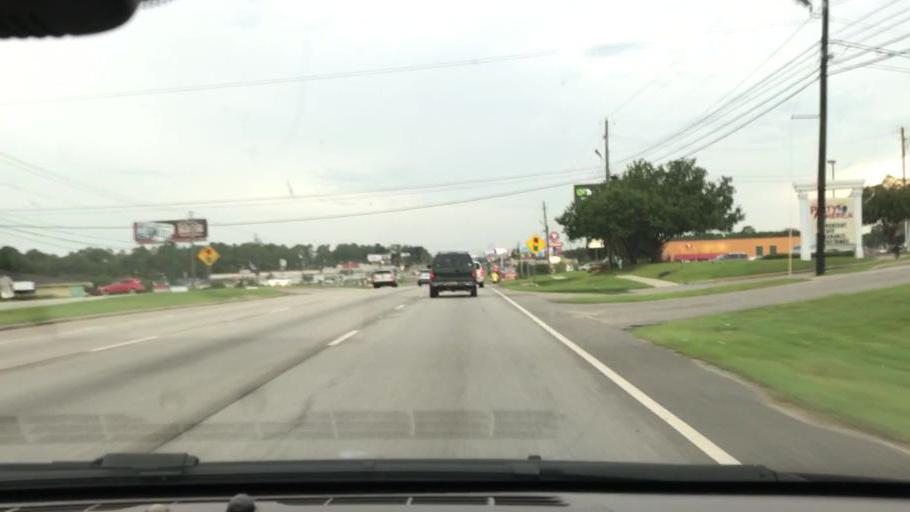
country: US
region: Alabama
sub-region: Houston County
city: Dothan
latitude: 31.2534
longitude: -85.4291
